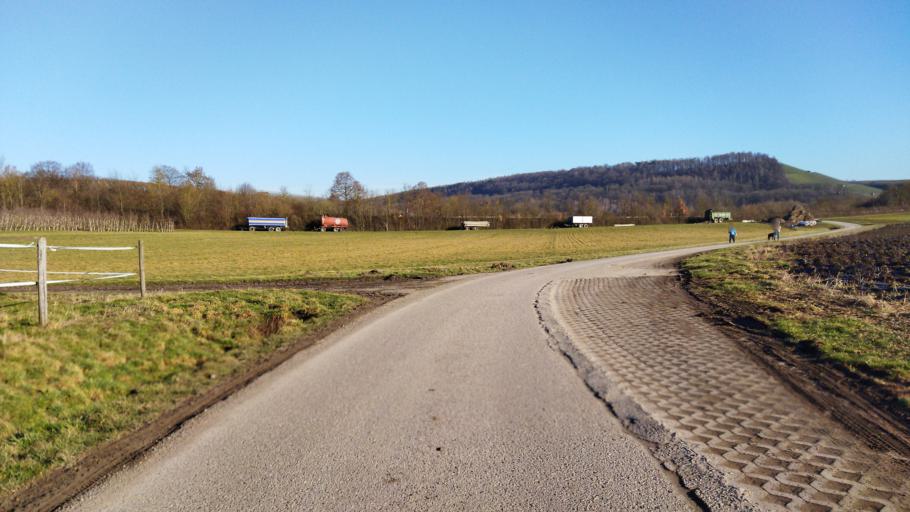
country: DE
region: Baden-Wuerttemberg
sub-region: Regierungsbezirk Stuttgart
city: Weinsberg
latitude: 49.1732
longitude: 9.2937
